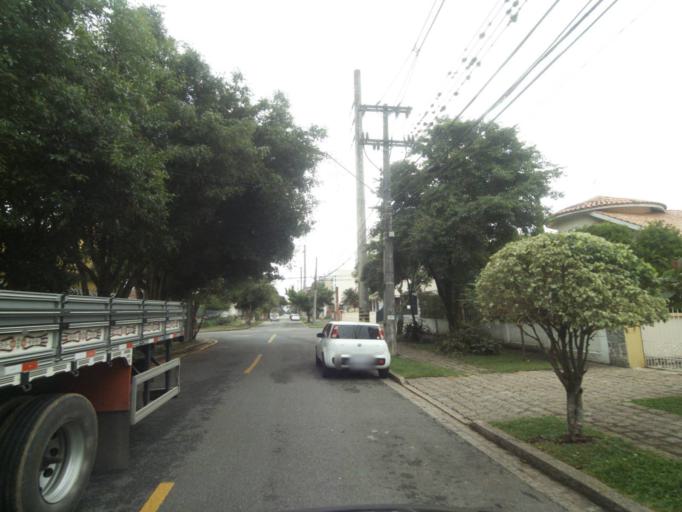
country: BR
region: Parana
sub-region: Curitiba
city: Curitiba
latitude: -25.4204
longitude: -49.2554
